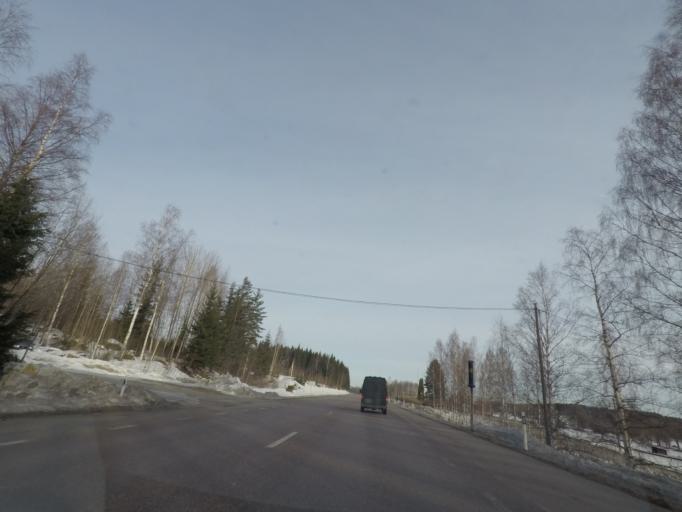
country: SE
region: Dalarna
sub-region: Smedjebackens Kommun
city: Smedjebacken
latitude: 60.1199
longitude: 15.4751
